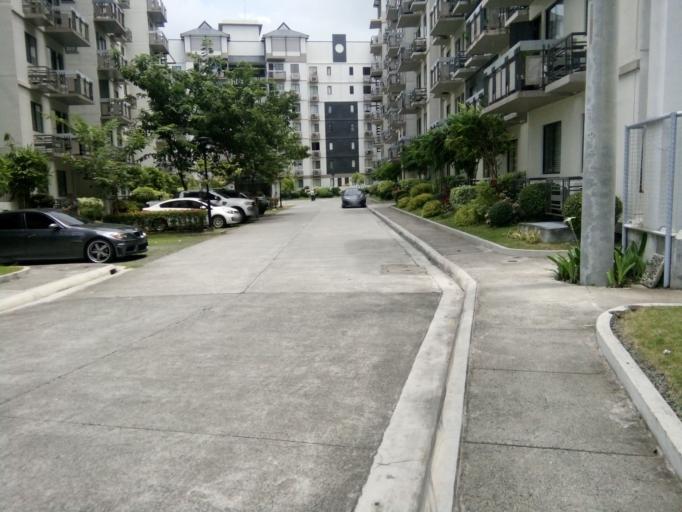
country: PH
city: Sambayanihan People's Village
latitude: 14.4375
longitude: 121.0439
